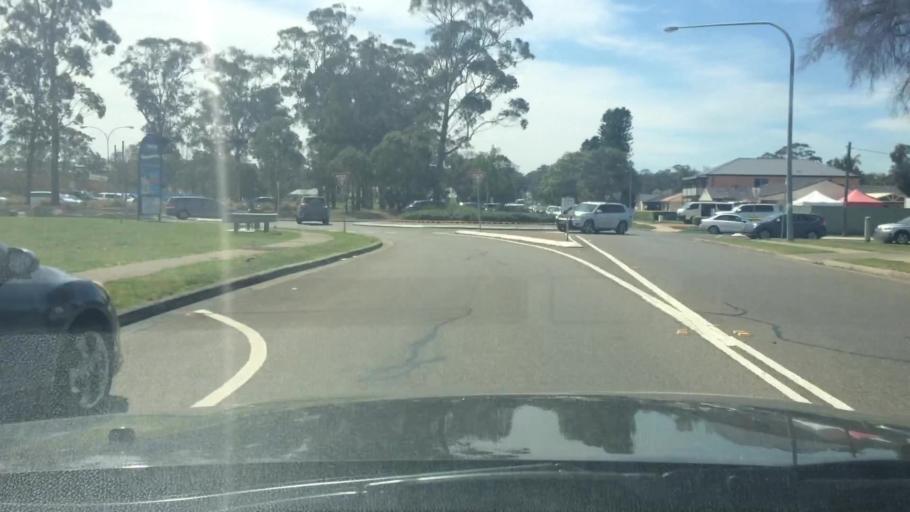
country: AU
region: New South Wales
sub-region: Fairfield
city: Cabramatta West
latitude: -33.8643
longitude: 150.8981
